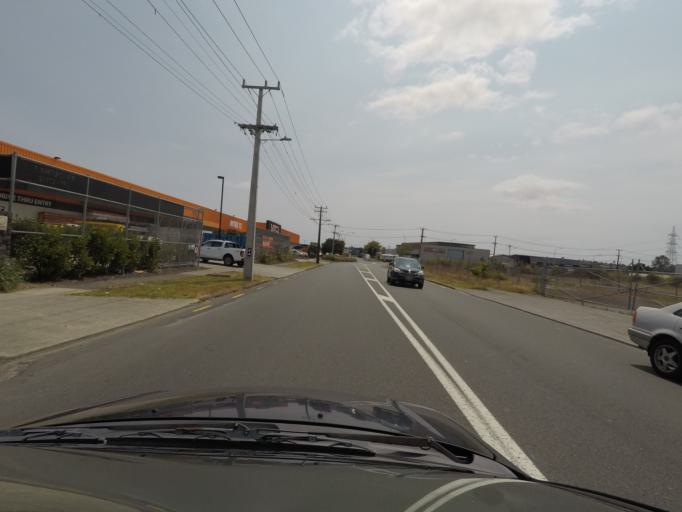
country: NZ
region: Auckland
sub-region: Auckland
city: Waitakere
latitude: -36.9129
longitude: 174.6880
